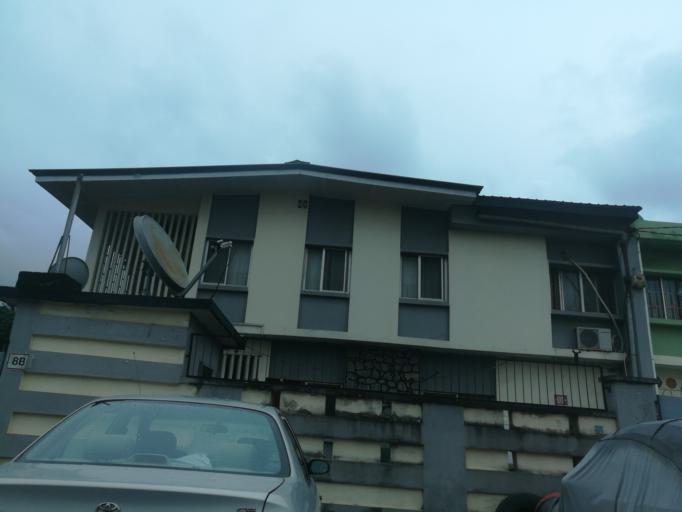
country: NG
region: Lagos
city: Agege
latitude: 6.6212
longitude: 3.3470
